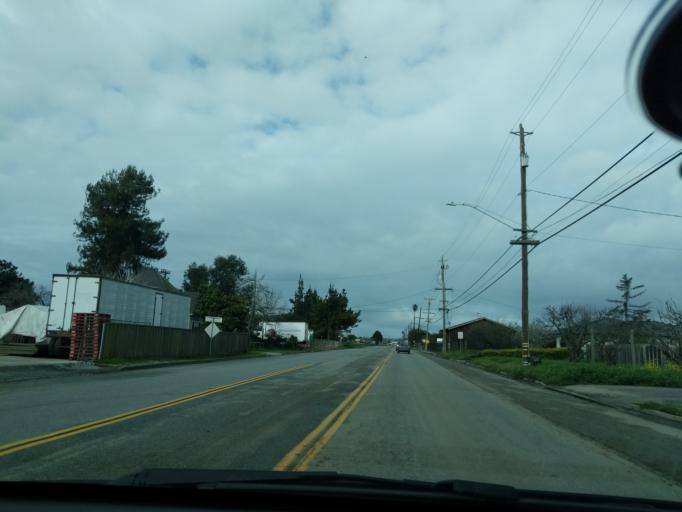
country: US
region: California
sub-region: Monterey County
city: Pajaro
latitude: 36.9043
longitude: -121.7368
